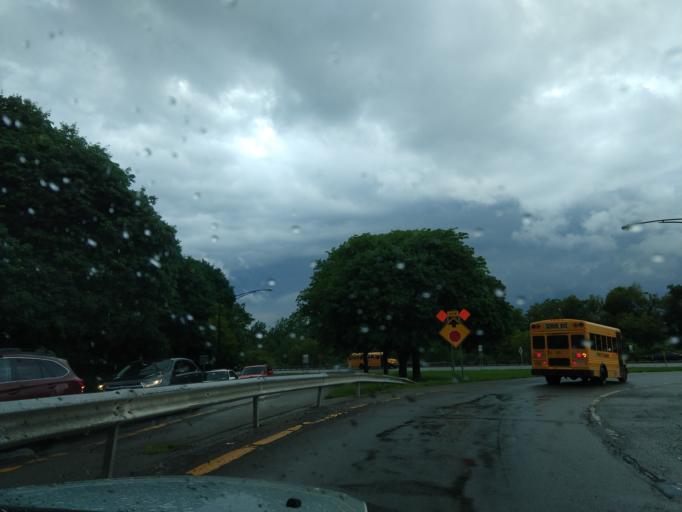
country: US
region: New York
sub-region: Erie County
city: Kenmore
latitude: 42.9355
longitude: -78.8889
